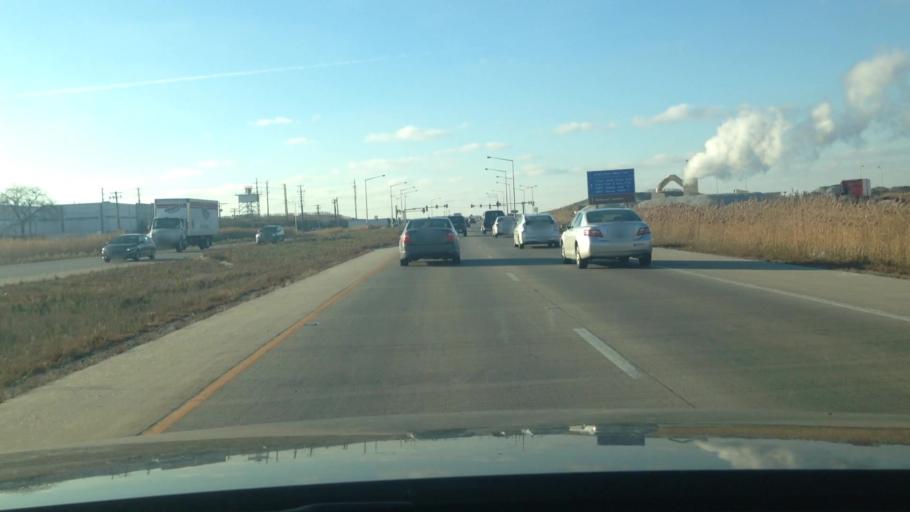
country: US
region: Illinois
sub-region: DuPage County
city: Bensenville
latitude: 41.9523
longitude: -87.9100
